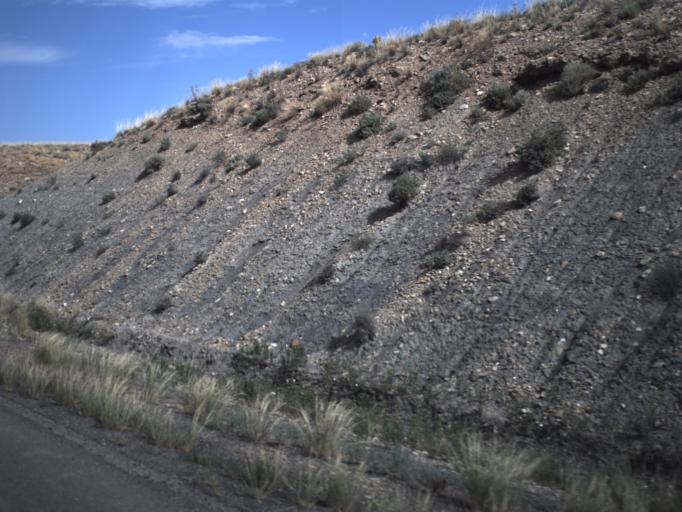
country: US
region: Utah
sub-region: Carbon County
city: East Carbon City
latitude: 39.5125
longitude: -110.5426
